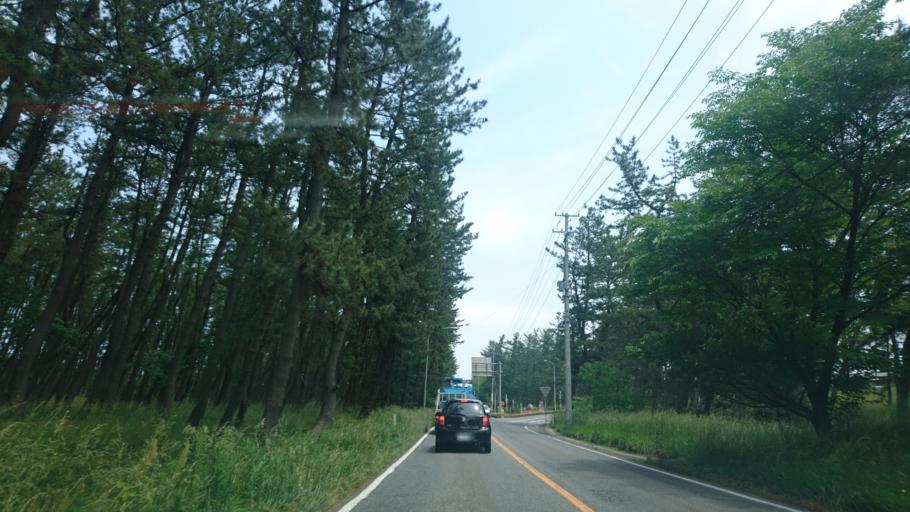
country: JP
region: Niigata
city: Shibata
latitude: 38.0337
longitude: 139.2964
